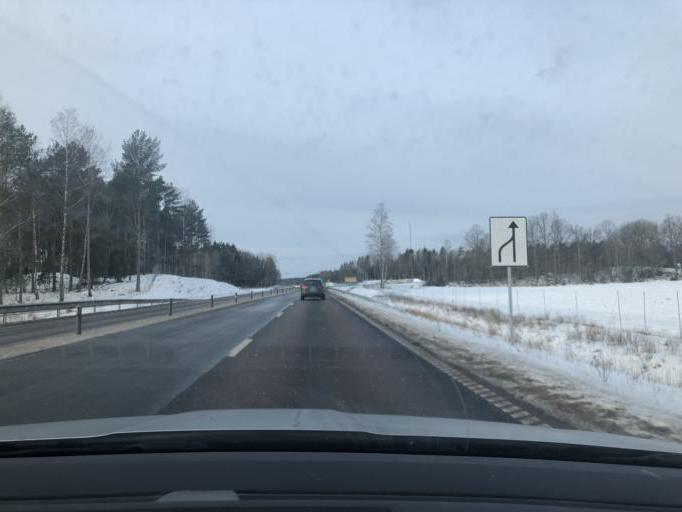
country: SE
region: OEstergoetland
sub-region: Motala Kommun
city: Ryd
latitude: 58.5873
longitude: 15.1476
